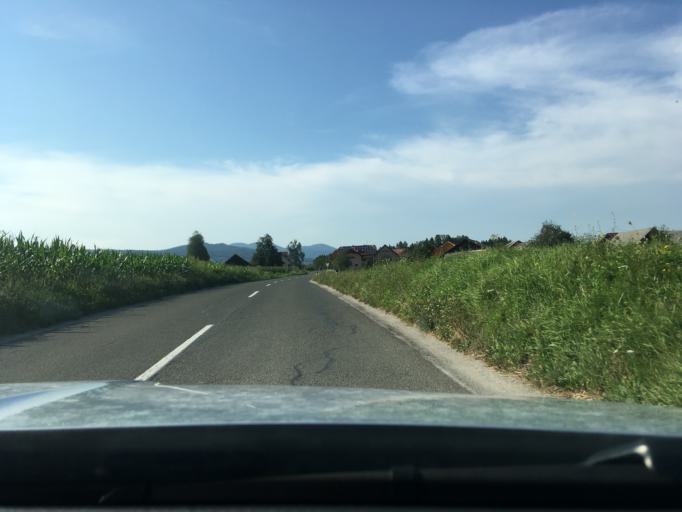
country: SI
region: Crnomelj
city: Crnomelj
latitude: 45.5391
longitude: 15.1611
